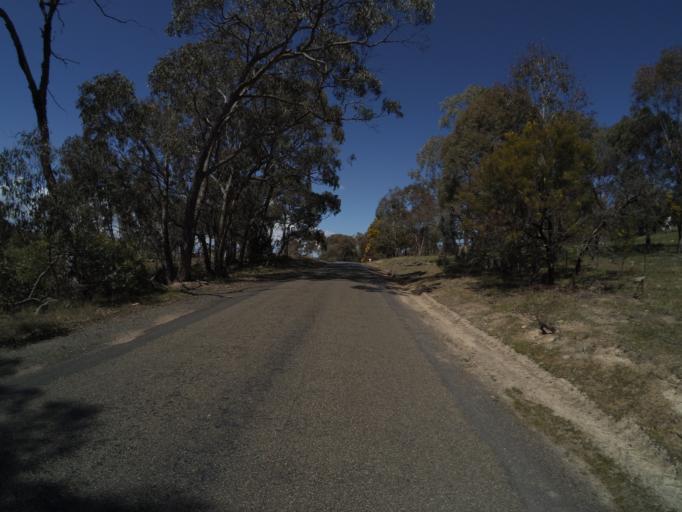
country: AU
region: Australian Capital Territory
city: Macquarie
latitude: -35.2038
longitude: 148.8992
